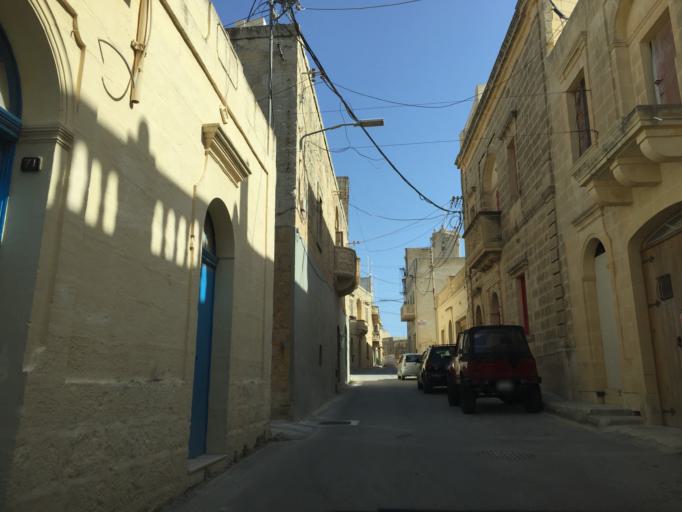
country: MT
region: L-Gharb
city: Gharb
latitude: 36.0612
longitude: 14.2089
